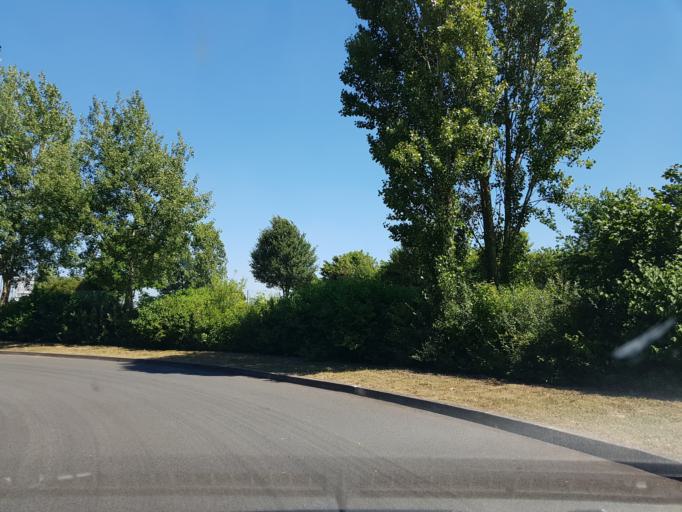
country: FR
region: Picardie
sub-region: Departement de la Somme
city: Doingt
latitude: 49.8387
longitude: 2.9922
